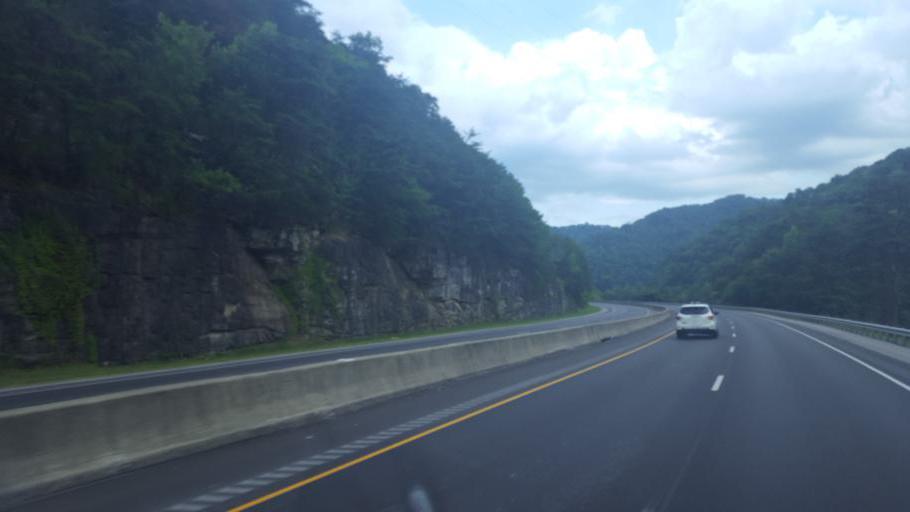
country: US
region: Kentucky
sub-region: Pike County
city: Pikeville
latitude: 37.3540
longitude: -82.5544
